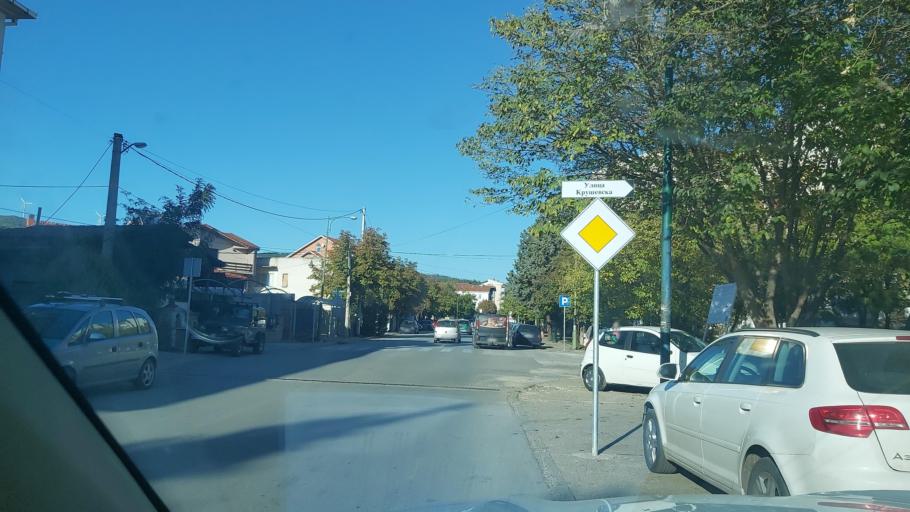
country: MK
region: Bogdanci
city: Bogdanci
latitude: 41.1992
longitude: 22.5713
